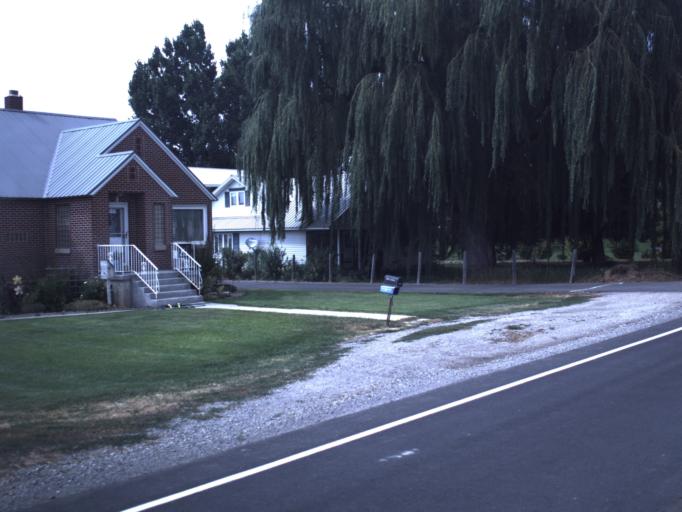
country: US
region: Utah
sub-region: Box Elder County
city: Garland
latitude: 41.8067
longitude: -112.1159
